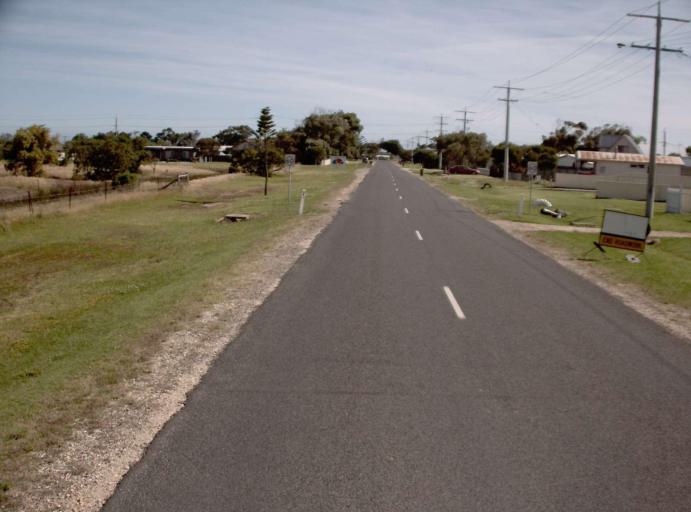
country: AU
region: Victoria
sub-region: Wellington
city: Sale
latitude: -38.3695
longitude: 147.1896
